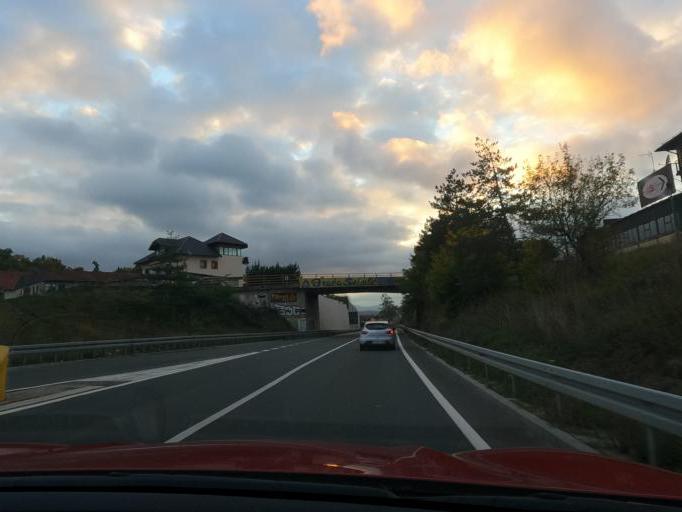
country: RS
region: Central Serbia
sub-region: Zlatiborski Okrug
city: Uzice
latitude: 43.8123
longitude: 19.7980
